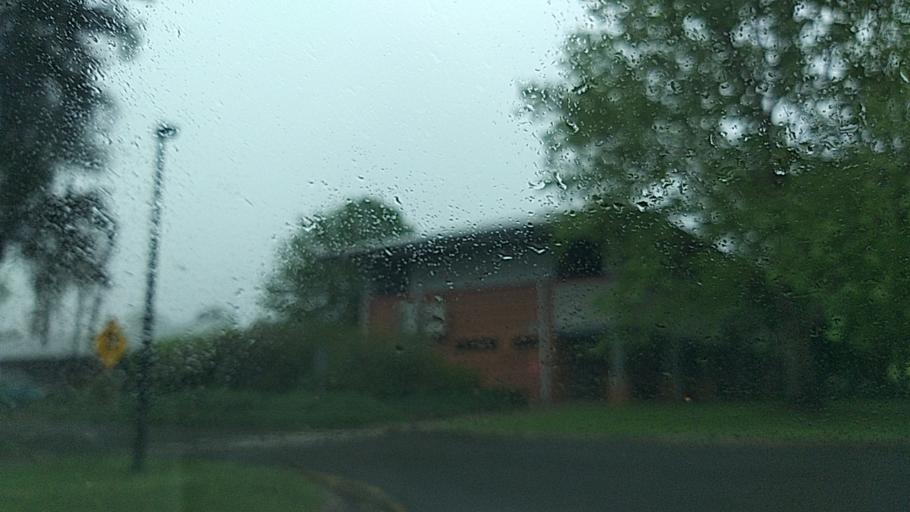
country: AU
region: New South Wales
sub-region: Hawkesbury
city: Richmond
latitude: -33.6114
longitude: 150.7541
